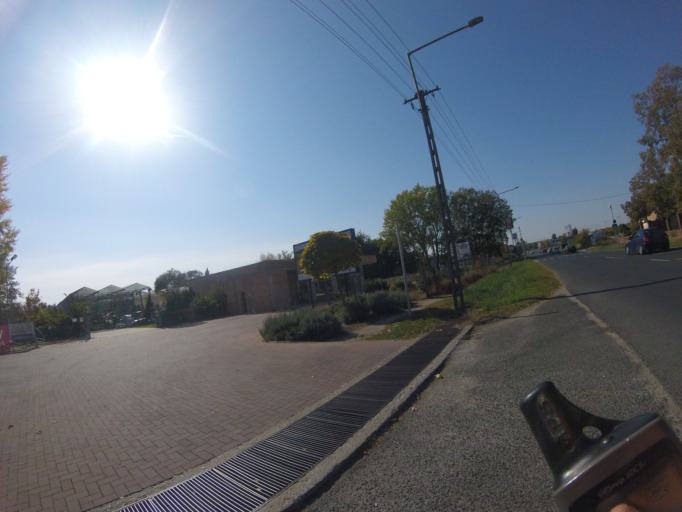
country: HU
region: Zala
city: Gyenesdias
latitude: 46.7730
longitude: 17.2700
